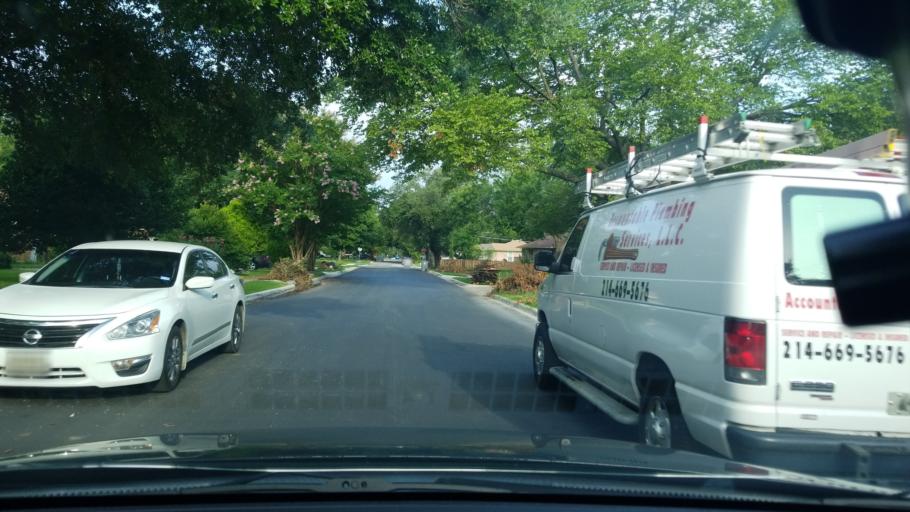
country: US
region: Texas
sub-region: Dallas County
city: Garland
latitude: 32.8296
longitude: -96.6595
